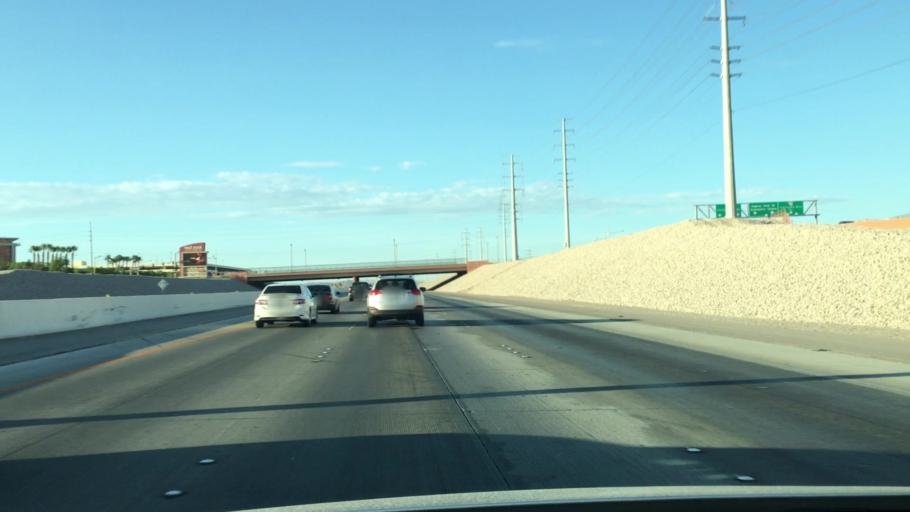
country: US
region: Nevada
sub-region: Clark County
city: Summerlin South
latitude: 36.1620
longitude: -115.3375
